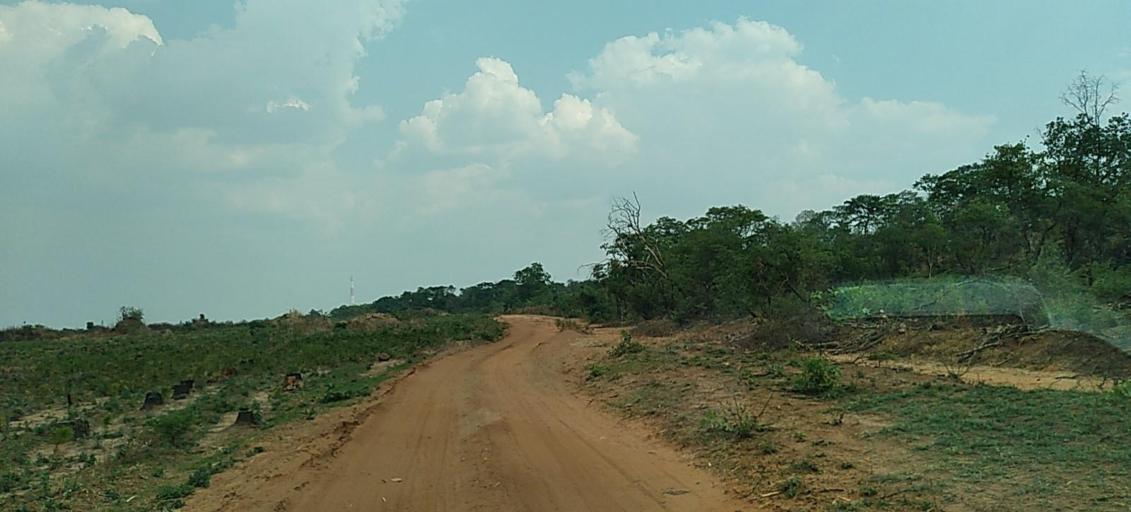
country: ZM
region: Copperbelt
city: Chingola
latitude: -12.7436
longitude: 27.7776
